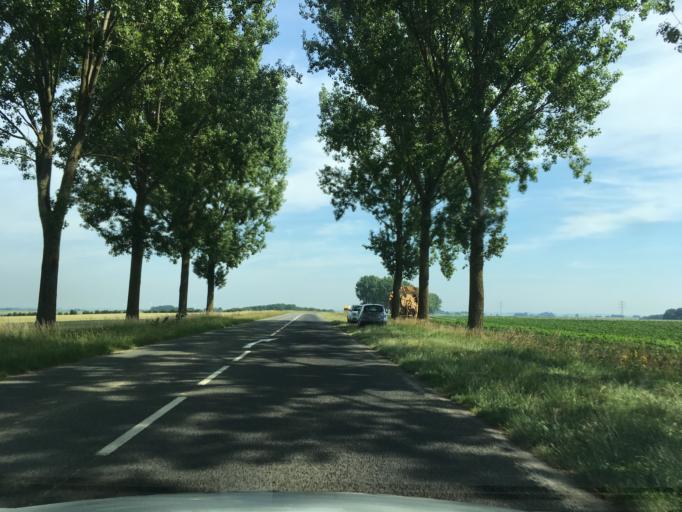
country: FR
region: Picardie
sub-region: Departement de la Somme
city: Chaulnes
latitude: 49.8545
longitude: 2.8787
